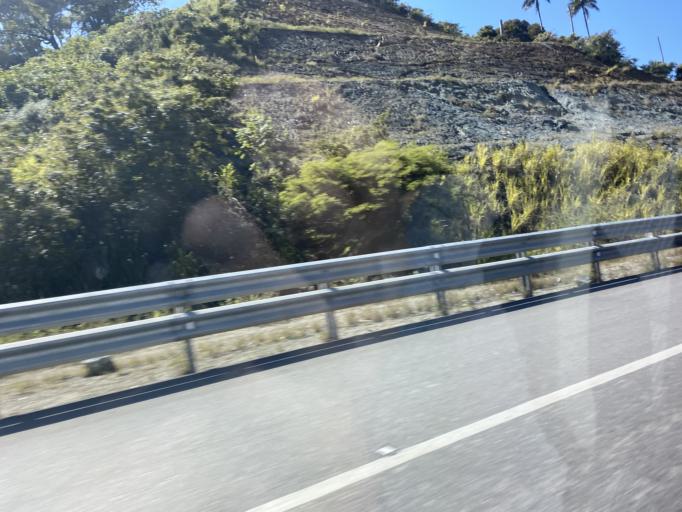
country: DO
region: Puerto Plata
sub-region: Puerto Plata
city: Puerto Plata
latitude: 19.8275
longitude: -70.7598
